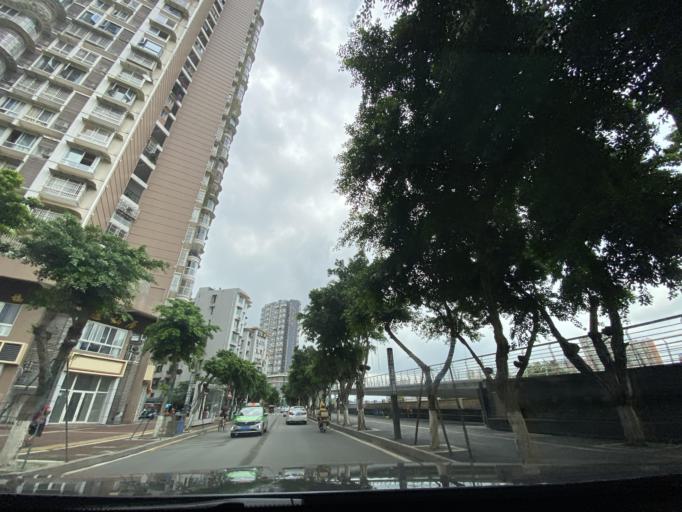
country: CN
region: Sichuan
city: Jiancheng
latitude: 30.3980
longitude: 104.5497
